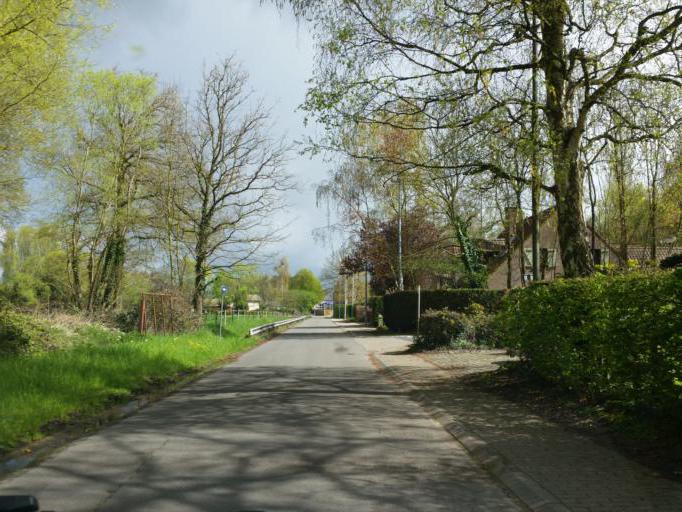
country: BE
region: Flanders
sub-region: Provincie Vlaams-Brabant
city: Boortmeerbeek
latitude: 50.9794
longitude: 4.5416
